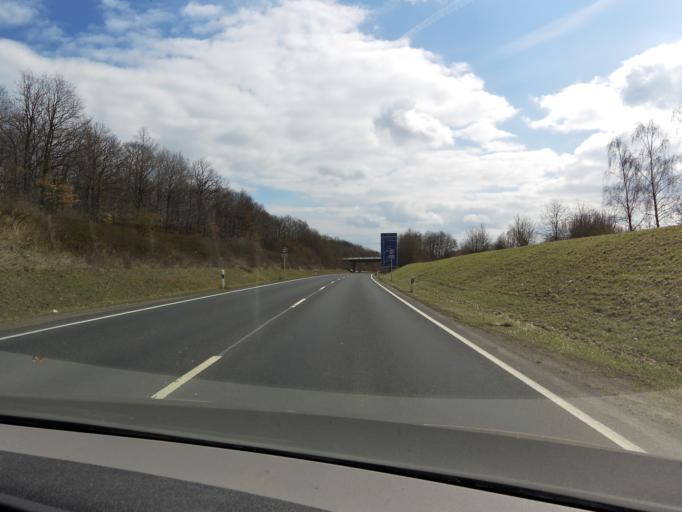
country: DE
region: Bavaria
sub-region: Regierungsbezirk Unterfranken
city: Werneck
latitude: 50.0066
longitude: 10.0678
